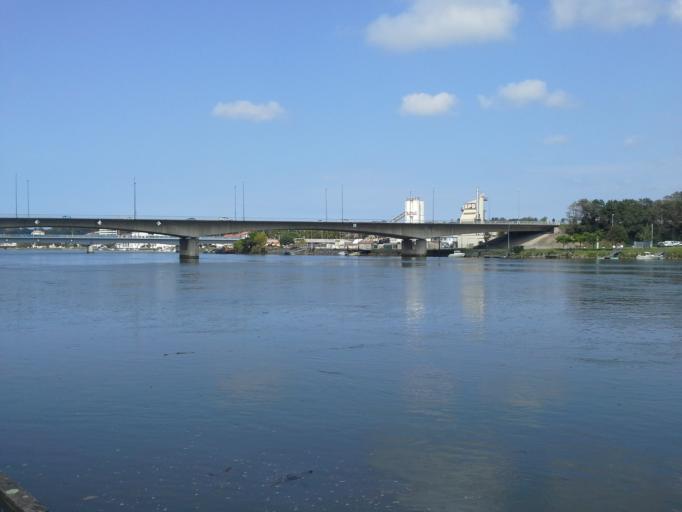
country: FR
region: Aquitaine
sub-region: Departement des Pyrenees-Atlantiques
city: Bayonne
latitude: 43.4858
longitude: -1.4606
